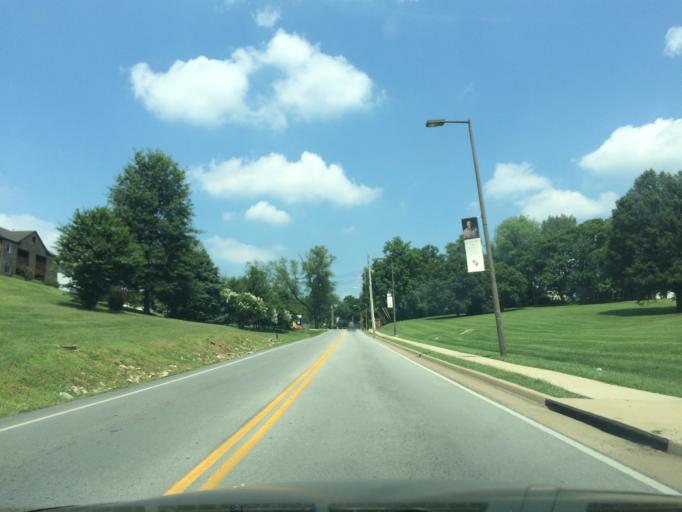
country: US
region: Kentucky
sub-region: Jefferson County
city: Audubon Park
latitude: 38.2185
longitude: -85.7089
